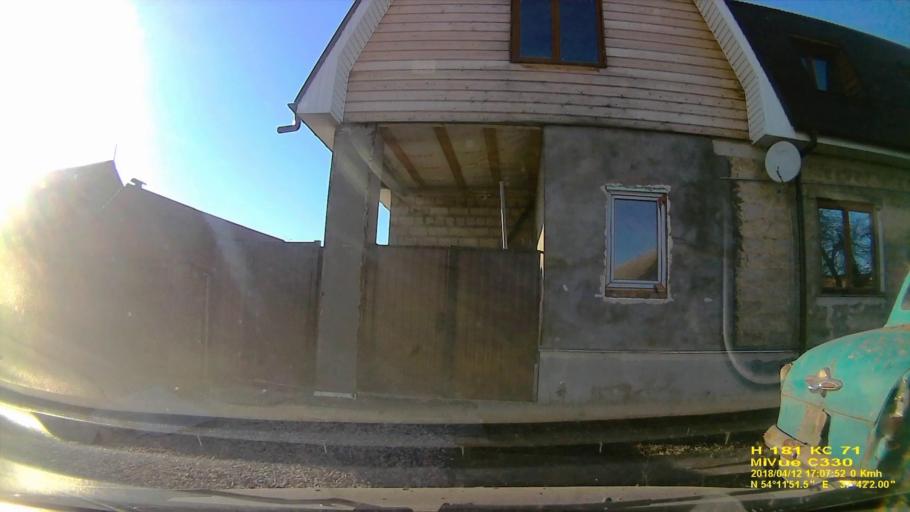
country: RU
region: Tula
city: Tula
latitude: 54.1977
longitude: 37.7005
